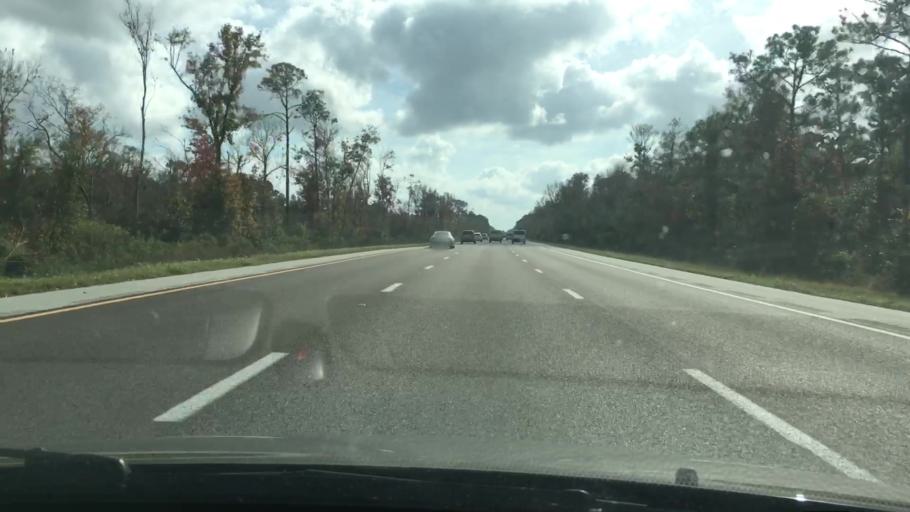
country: US
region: Florida
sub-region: Volusia County
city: Edgewater
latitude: 28.9244
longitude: -80.9389
